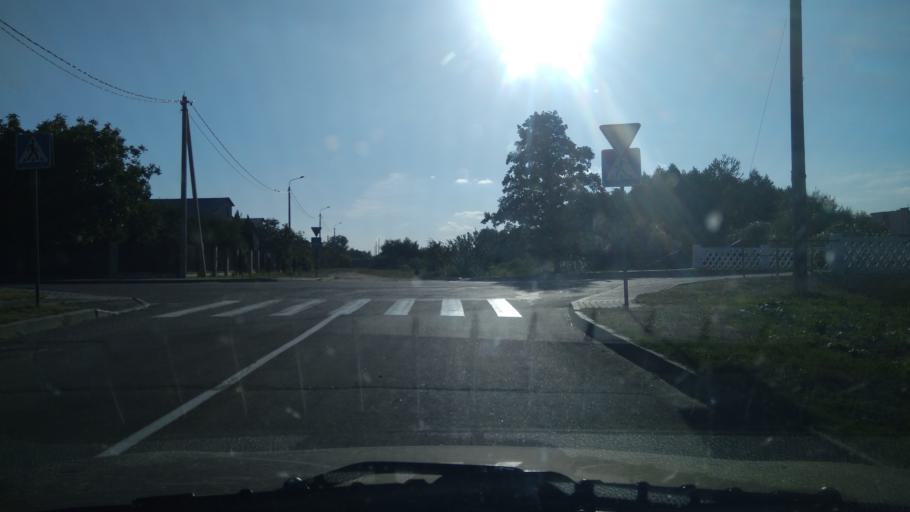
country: BY
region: Brest
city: Byaroza
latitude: 52.5373
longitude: 24.9787
